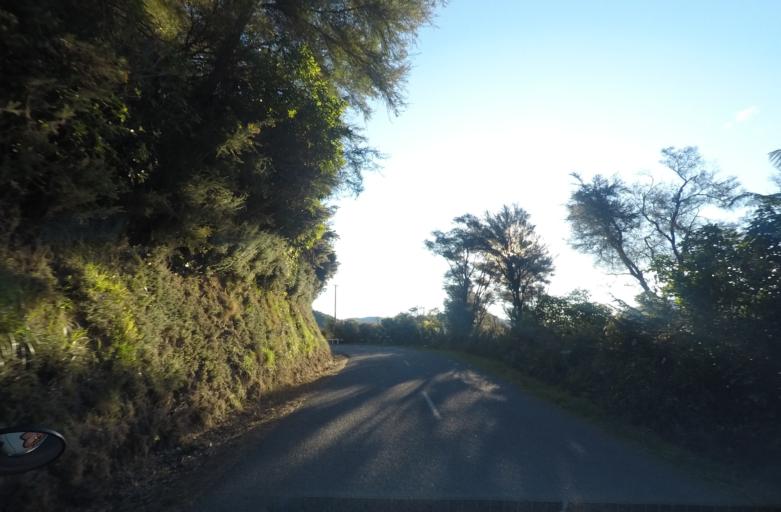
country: NZ
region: Marlborough
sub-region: Marlborough District
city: Picton
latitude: -41.2737
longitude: 173.9689
